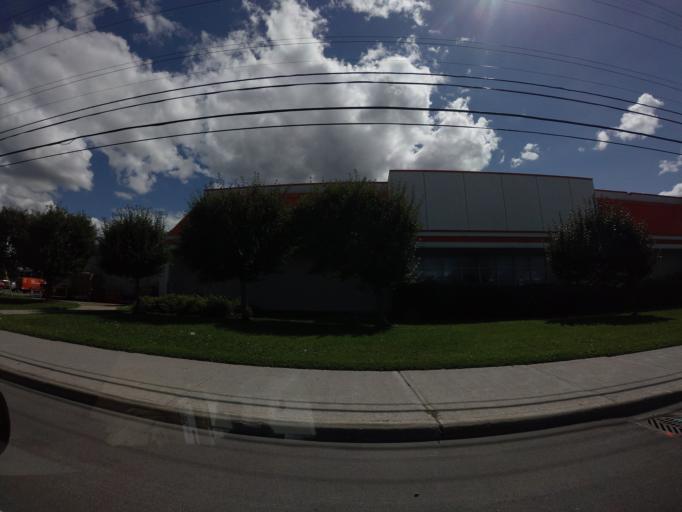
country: CA
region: Ontario
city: Bells Corners
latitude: 45.3531
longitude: -75.7584
